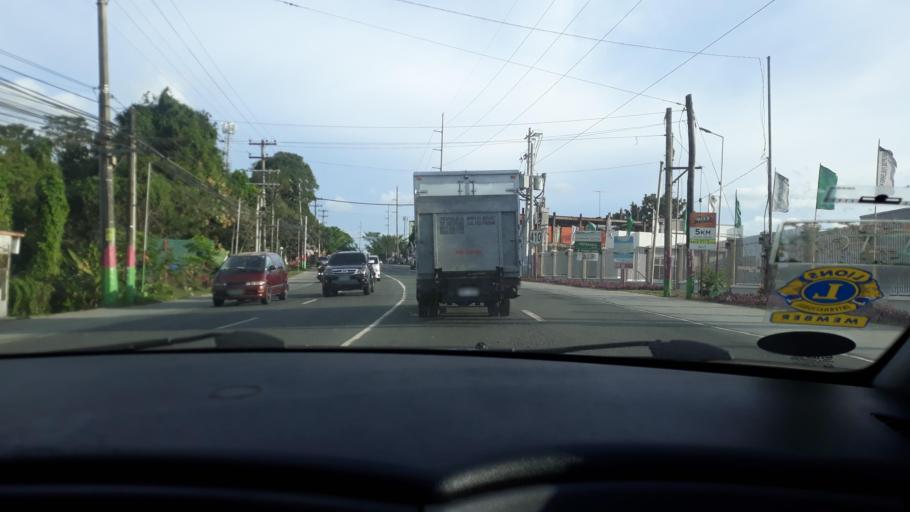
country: PH
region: Calabarzon
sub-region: Province of Cavite
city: Biga
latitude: 14.2623
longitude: 120.9693
